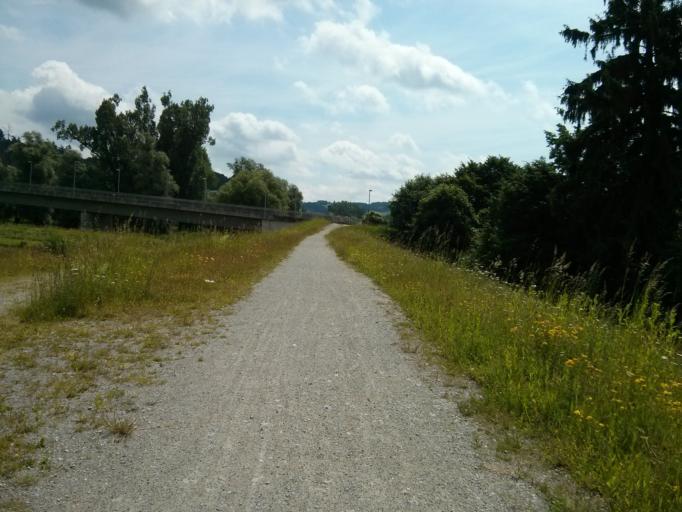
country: DE
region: Bavaria
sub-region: Lower Bavaria
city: Deggendorf
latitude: 48.8230
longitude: 12.9566
